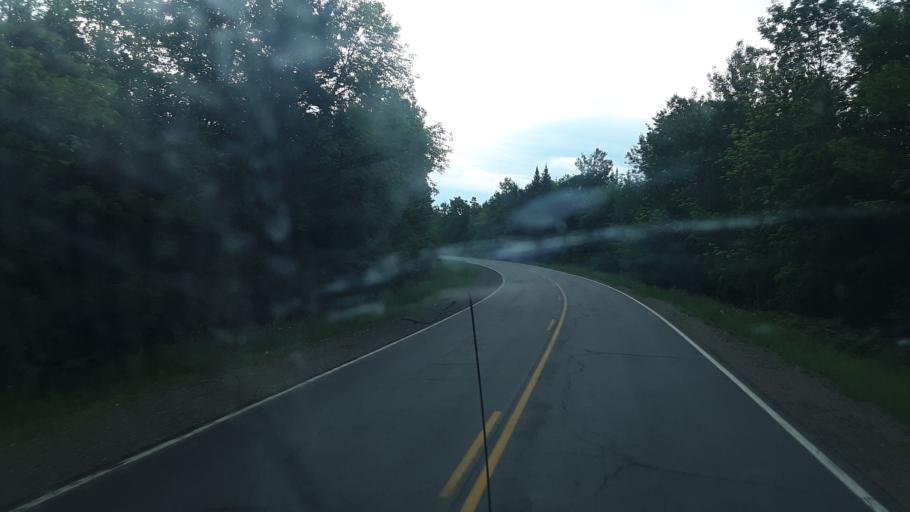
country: US
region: Maine
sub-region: Penobscot County
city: Medway
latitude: 45.6865
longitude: -68.2831
